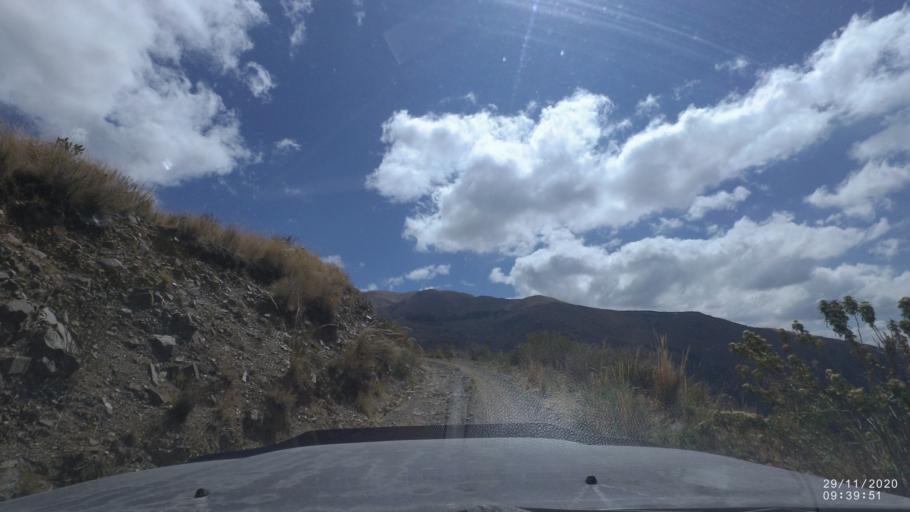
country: BO
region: Cochabamba
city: Cochabamba
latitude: -17.3043
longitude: -66.1814
